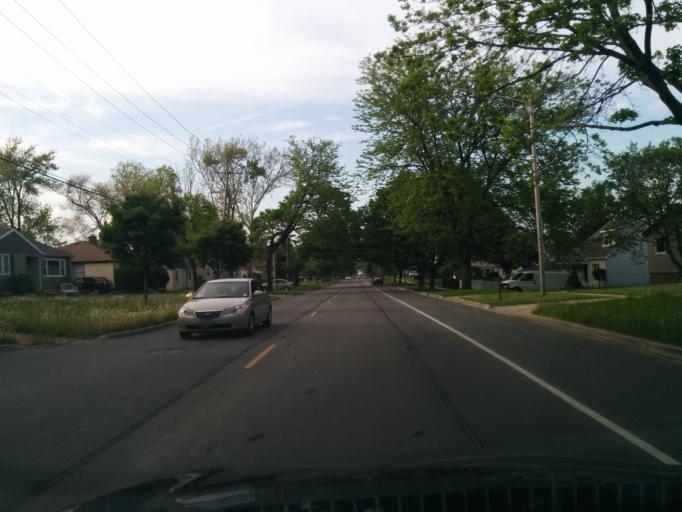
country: US
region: Illinois
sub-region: DuPage County
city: Lombard
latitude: 41.8982
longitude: -88.0082
